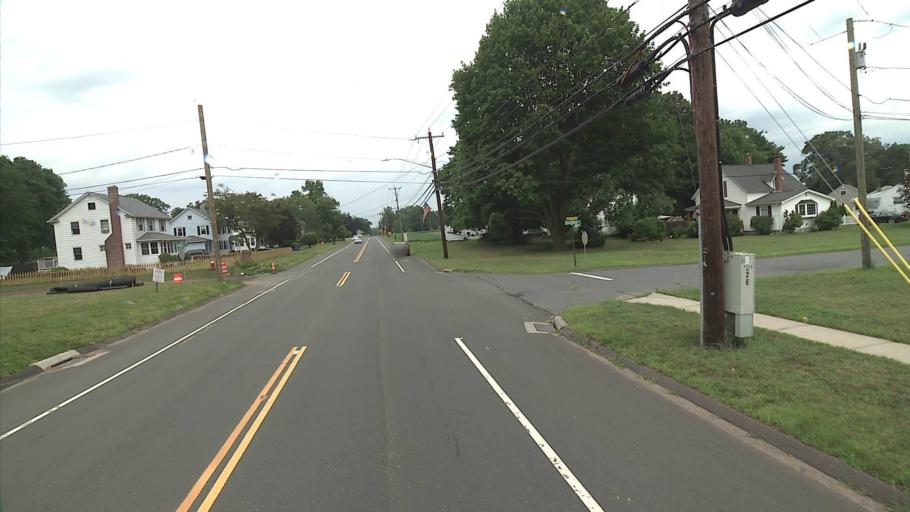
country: US
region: Connecticut
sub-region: Middlesex County
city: Cromwell
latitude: 41.6271
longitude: -72.6520
